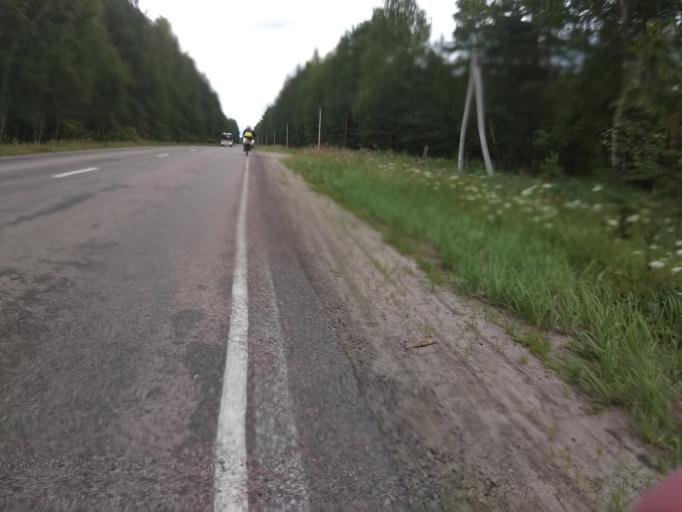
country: RU
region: Moskovskaya
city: Misheronskiy
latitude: 55.6108
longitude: 39.7165
